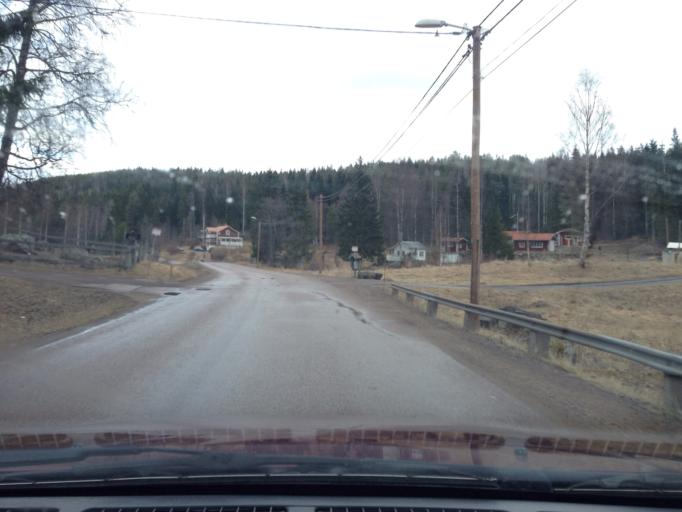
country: SE
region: Dalarna
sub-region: Ludvika Kommun
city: Ludvika
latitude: 60.1548
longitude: 15.2630
